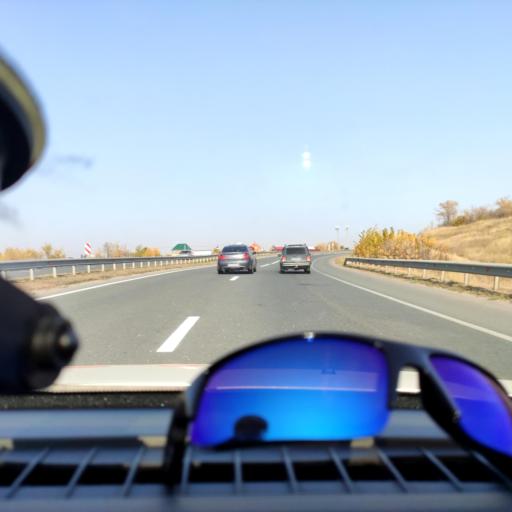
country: RU
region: Samara
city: Novokuybyshevsk
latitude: 53.0611
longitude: 50.0196
